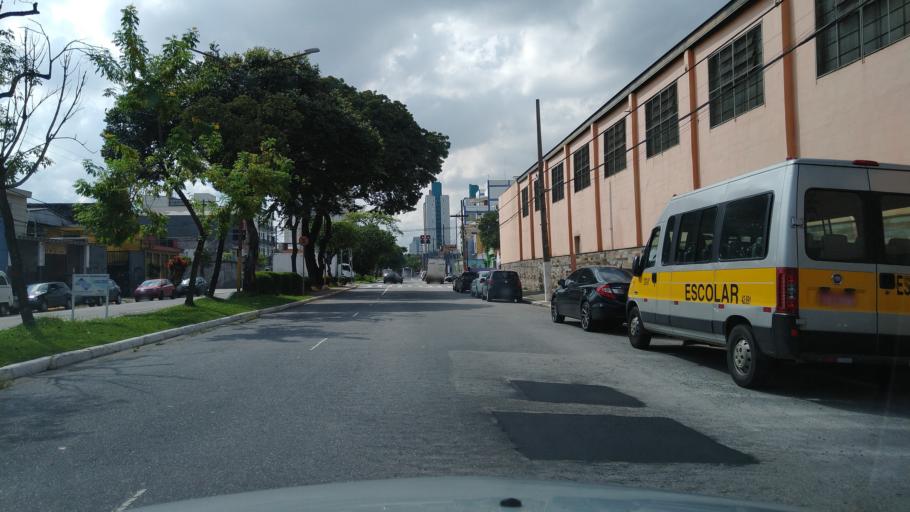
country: BR
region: Sao Paulo
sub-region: Guarulhos
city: Guarulhos
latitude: -23.5231
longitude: -46.5682
